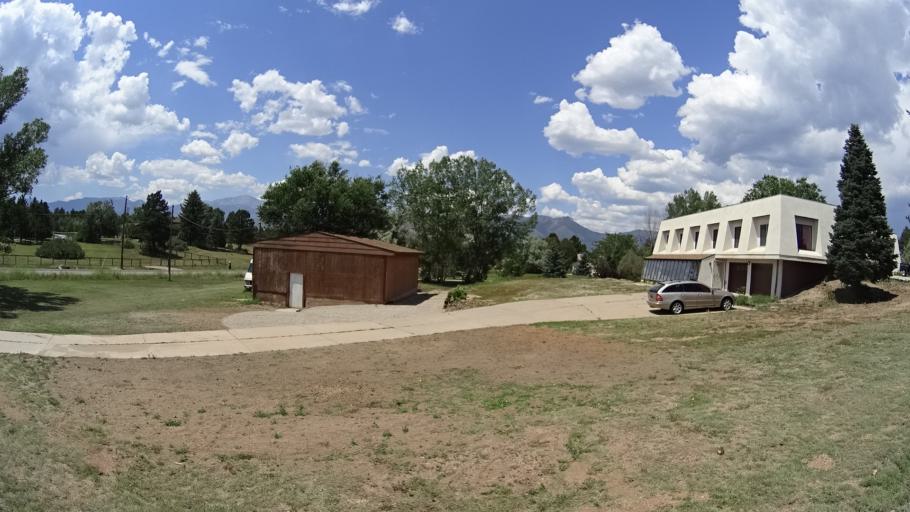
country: US
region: Colorado
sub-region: El Paso County
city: Air Force Academy
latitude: 38.9370
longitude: -104.8031
